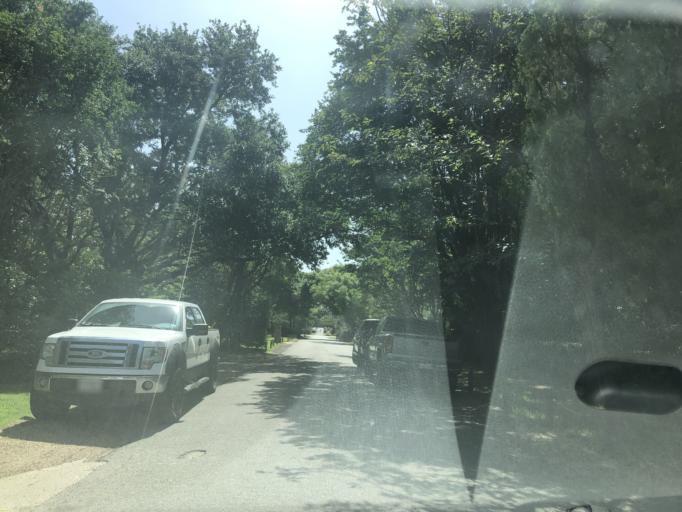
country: US
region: Texas
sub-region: Dallas County
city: University Park
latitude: 32.8771
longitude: -96.8162
